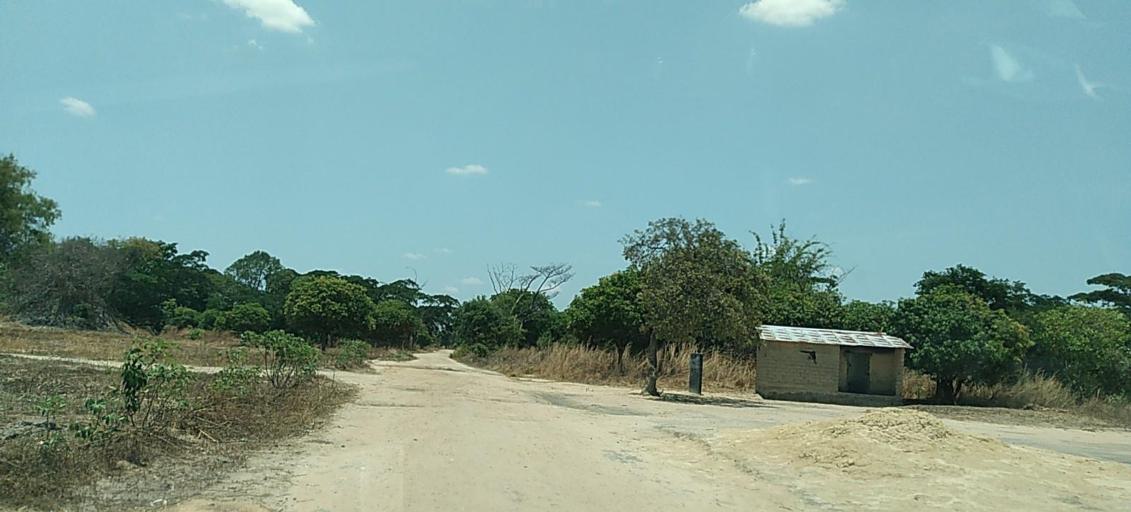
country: ZM
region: Copperbelt
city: Luanshya
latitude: -13.0775
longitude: 28.4051
